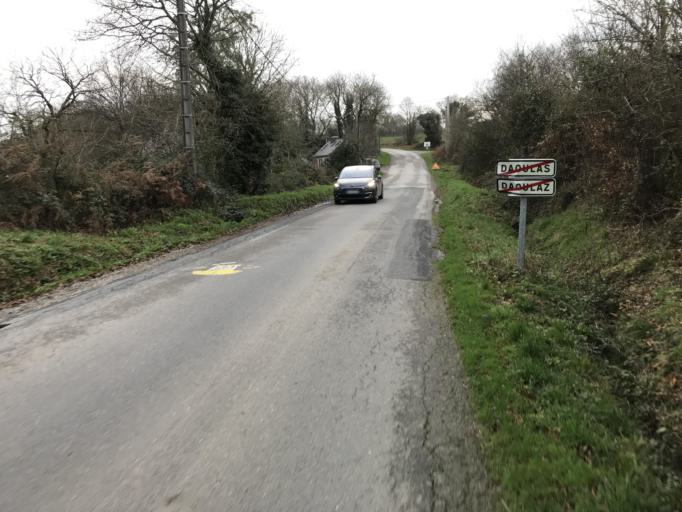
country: FR
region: Brittany
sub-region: Departement du Finistere
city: Daoulas
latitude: 48.3611
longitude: -4.2703
